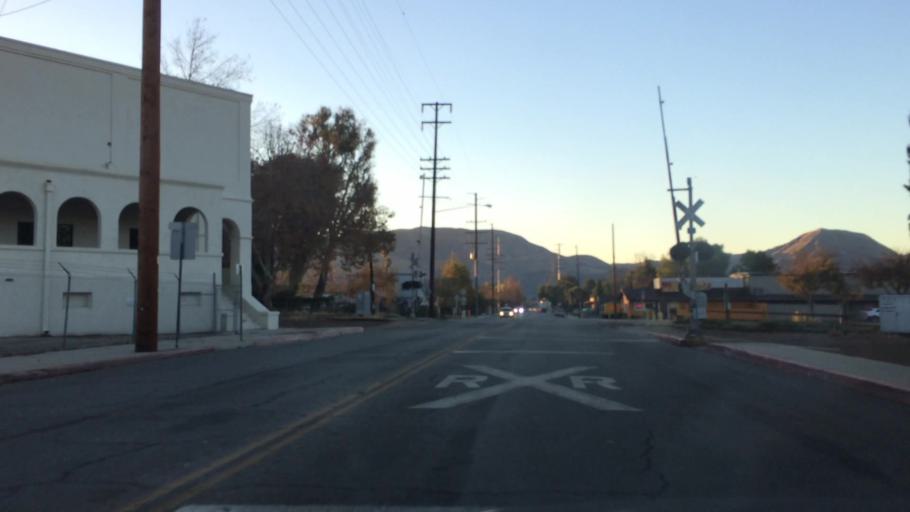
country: US
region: California
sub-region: Ventura County
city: Fillmore
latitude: 34.3997
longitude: -118.9185
